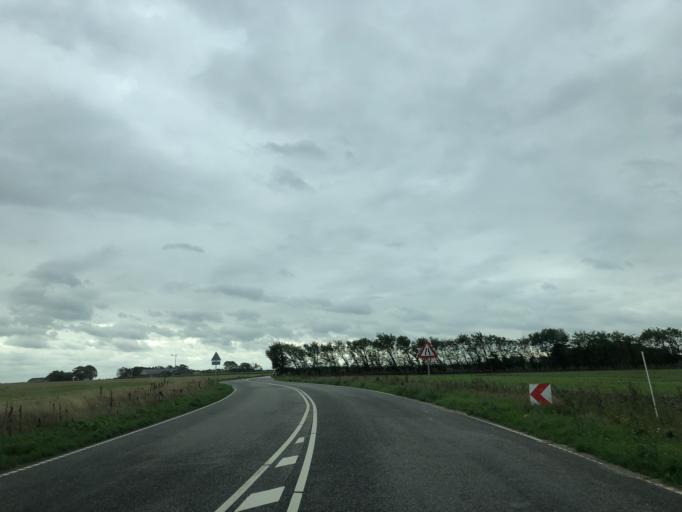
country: DK
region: Central Jutland
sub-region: Herning Kommune
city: Snejbjerg
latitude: 56.1520
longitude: 8.8931
